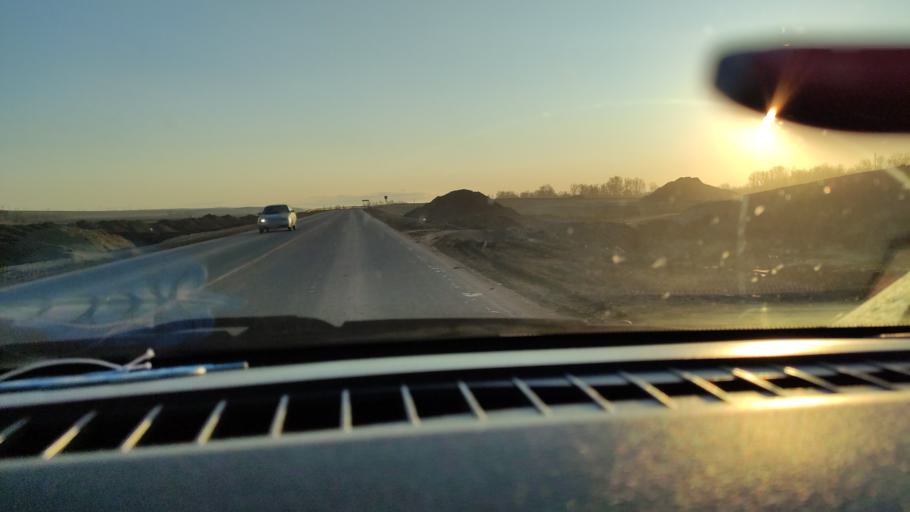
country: RU
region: Saratov
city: Sinodskoye
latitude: 52.0136
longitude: 46.6908
